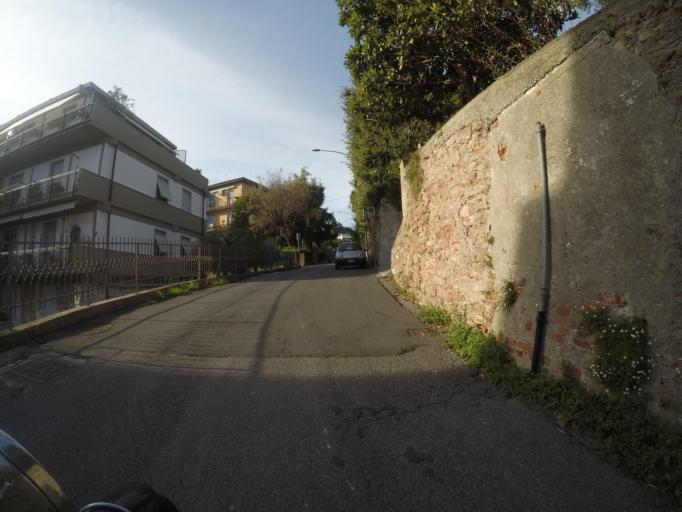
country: IT
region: Tuscany
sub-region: Provincia di Massa-Carrara
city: Carrara
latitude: 44.0782
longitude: 10.0934
